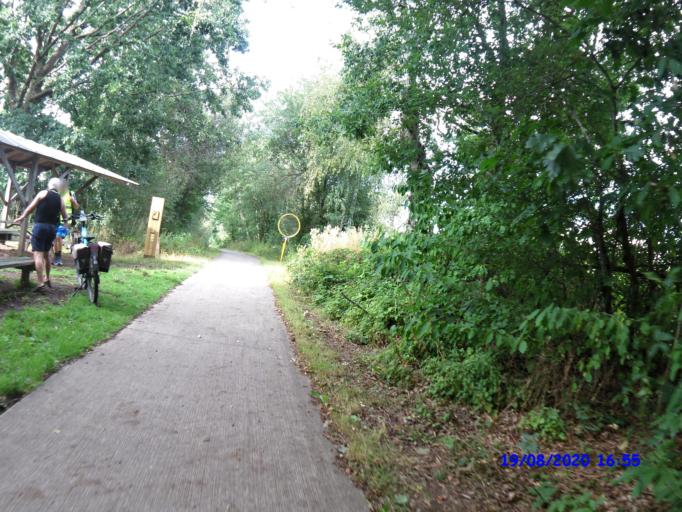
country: BE
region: Flanders
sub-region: Provincie Limburg
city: Nieuwerkerken
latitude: 50.8635
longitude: 5.2087
